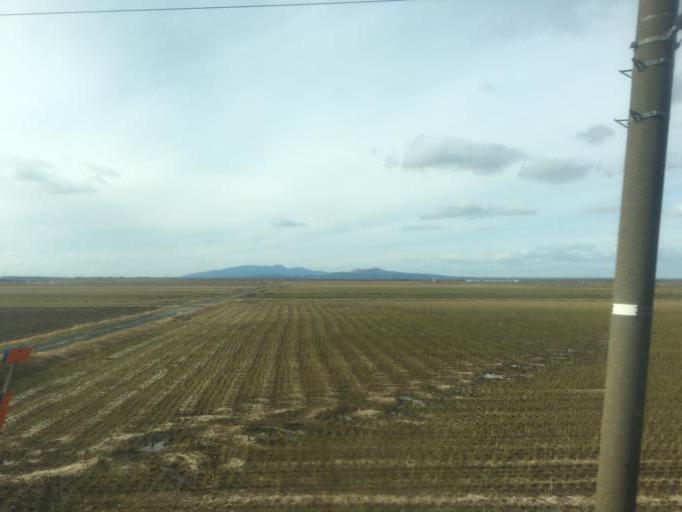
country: JP
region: Akita
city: Tenno
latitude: 39.9073
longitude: 140.0752
